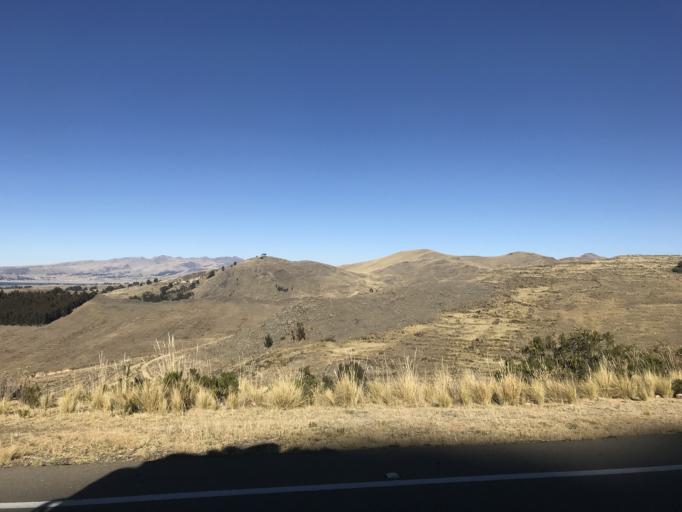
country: PE
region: Puno
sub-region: Yunguyo
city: Yunguyo
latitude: -16.1881
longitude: -68.9779
